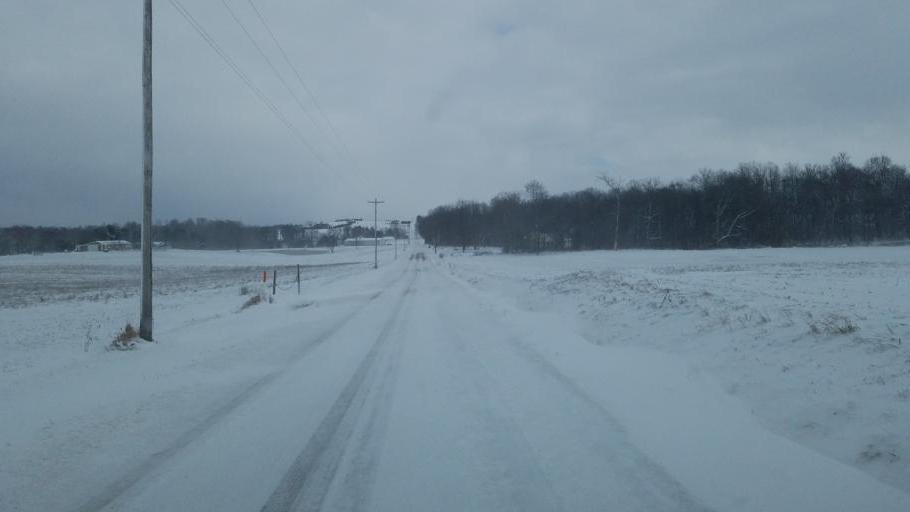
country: US
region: Ohio
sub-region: Richland County
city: Lexington
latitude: 40.6011
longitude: -82.6221
